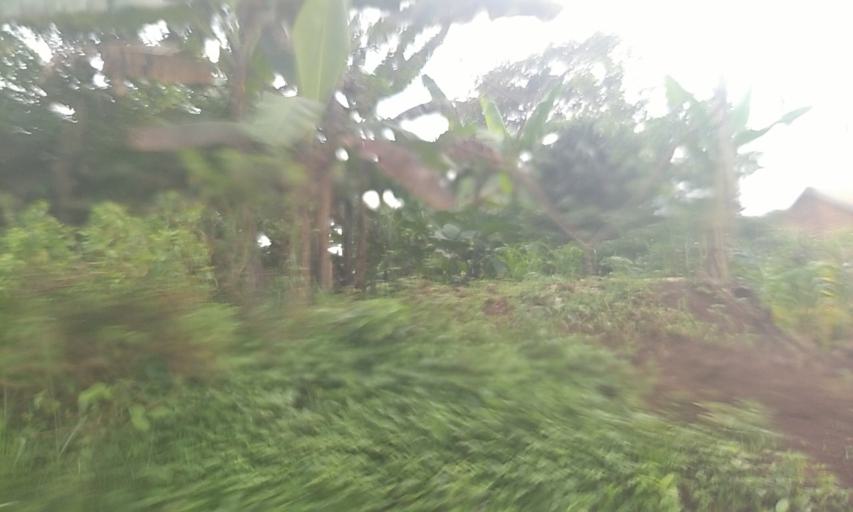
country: UG
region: Central Region
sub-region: Wakiso District
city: Wakiso
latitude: 0.3568
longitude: 32.4558
